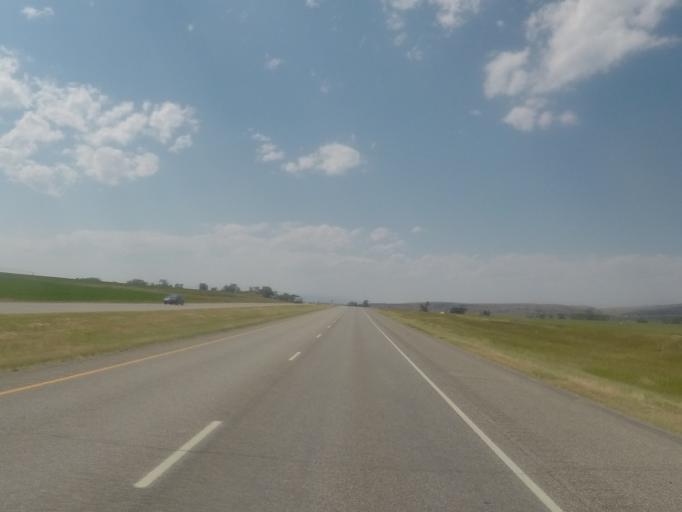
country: US
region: Montana
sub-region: Gallatin County
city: Manhattan
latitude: 45.8685
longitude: -111.3767
